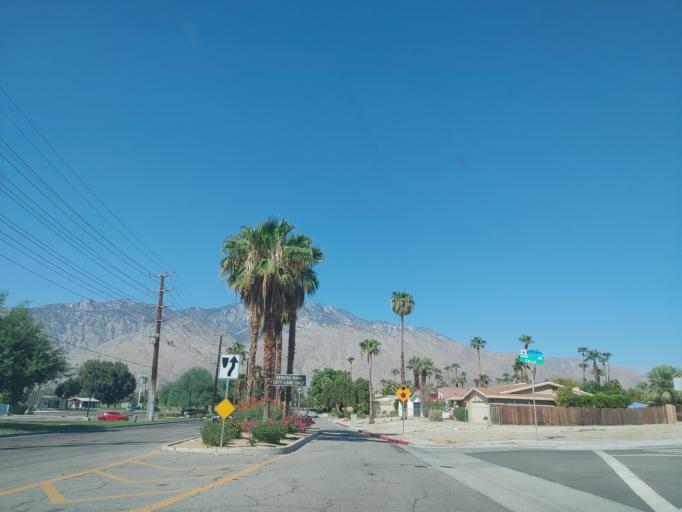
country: US
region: California
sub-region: Riverside County
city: Cathedral City
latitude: 33.8087
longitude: -116.5013
